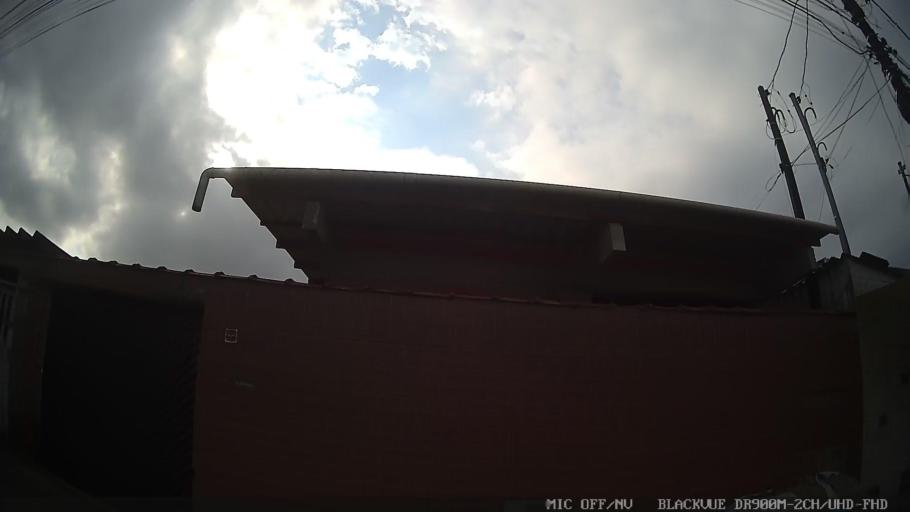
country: BR
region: Sao Paulo
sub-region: Guaruja
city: Guaruja
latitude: -23.9604
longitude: -46.2772
